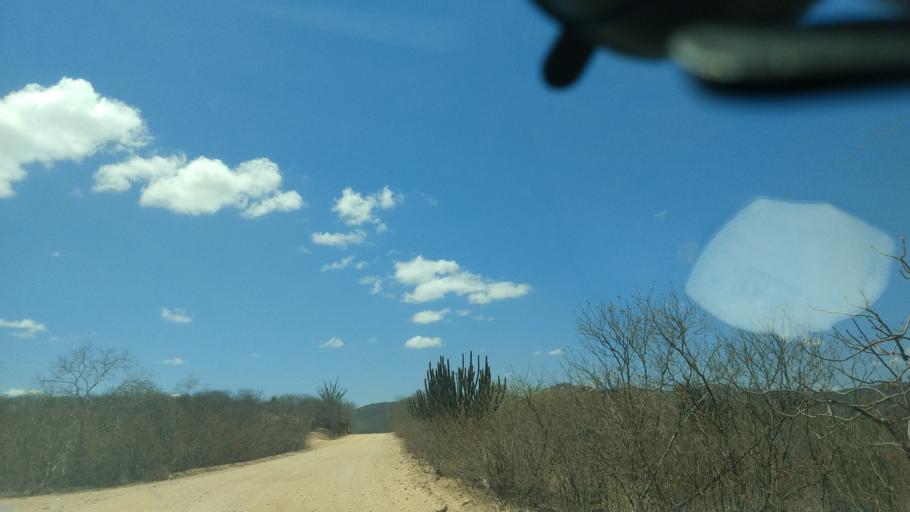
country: BR
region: Rio Grande do Norte
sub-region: Cerro Cora
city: Cerro Cora
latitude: -6.0138
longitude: -36.3033
